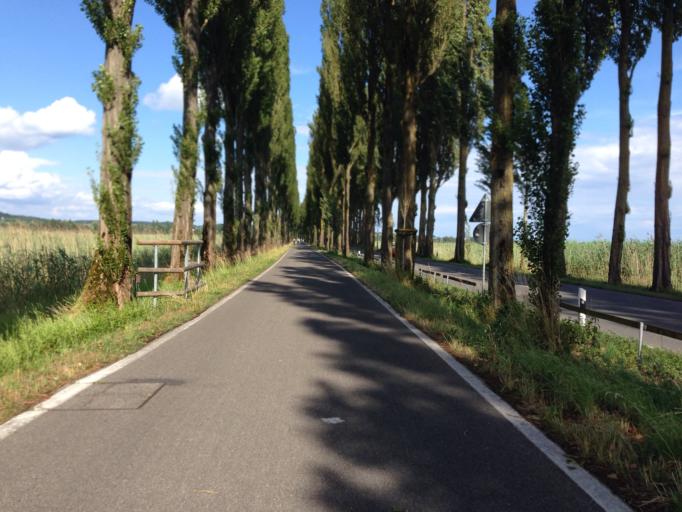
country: CH
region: Thurgau
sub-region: Kreuzlingen District
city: Ermatingen
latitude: 47.6867
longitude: 9.1019
